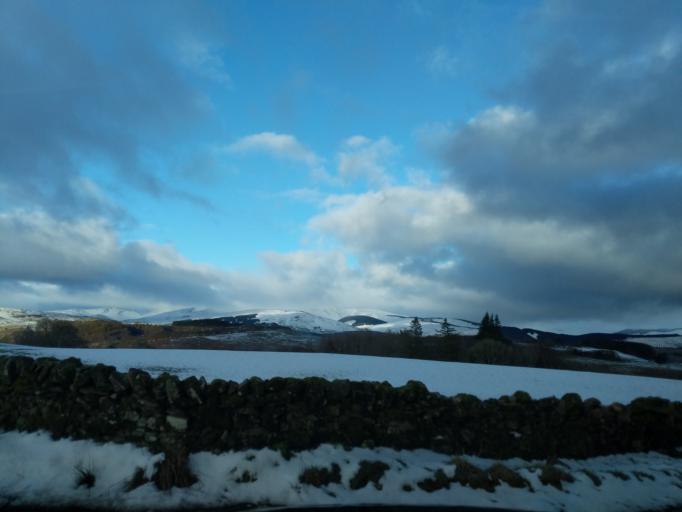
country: GB
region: Scotland
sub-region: Dumfries and Galloway
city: Moffat
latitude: 55.3218
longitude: -3.4807
